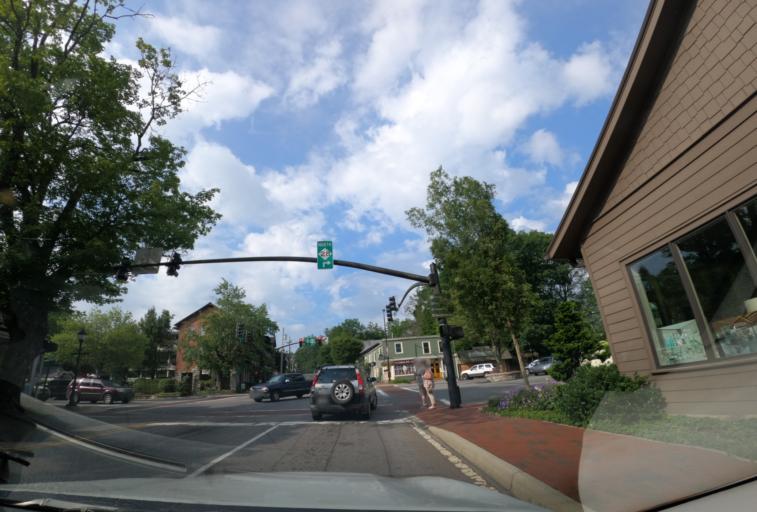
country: US
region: North Carolina
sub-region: Macon County
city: Franklin
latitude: 35.0528
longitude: -83.1971
